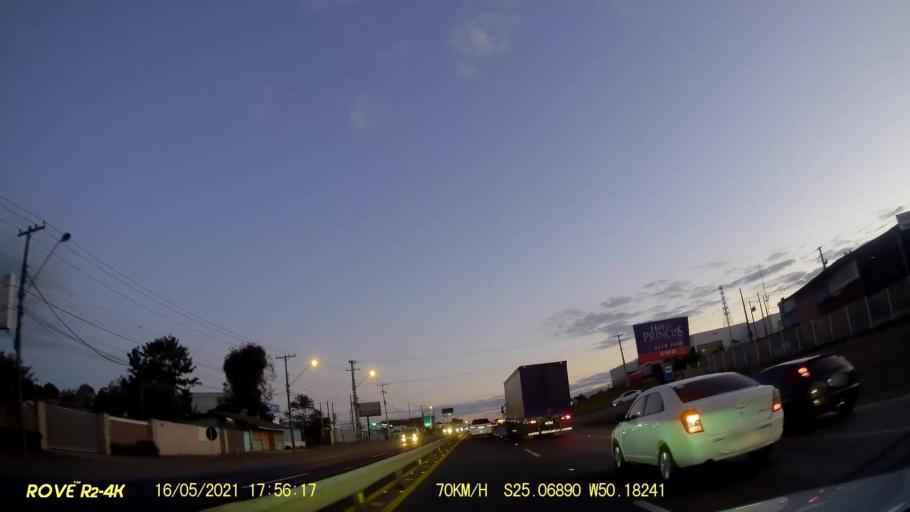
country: BR
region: Parana
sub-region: Ponta Grossa
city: Ponta Grossa
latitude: -25.0689
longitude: -50.1824
